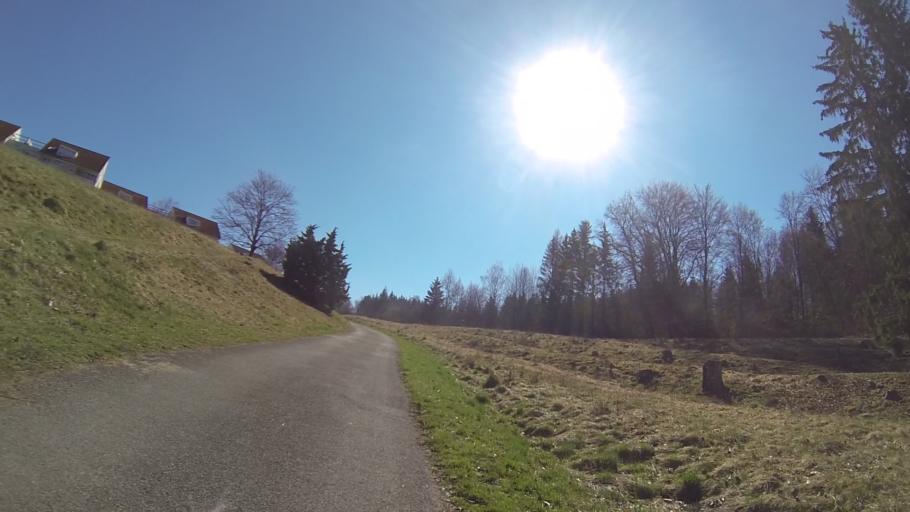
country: DE
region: Baden-Wuerttemberg
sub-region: Regierungsbezirk Stuttgart
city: Heidenheim an der Brenz
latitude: 48.6743
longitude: 10.1831
